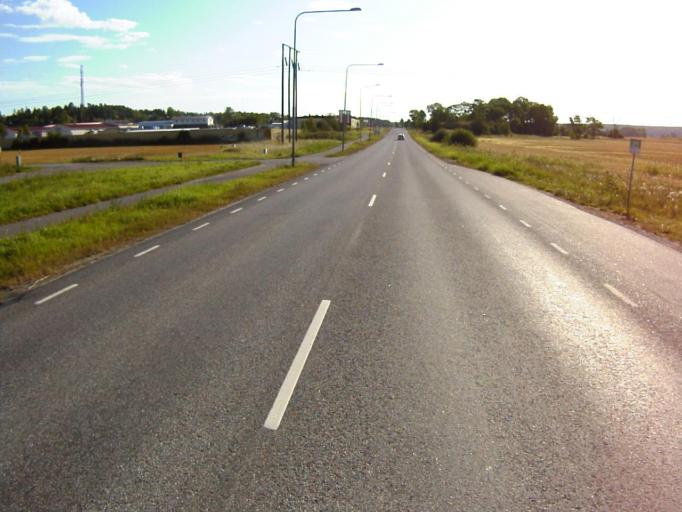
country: SE
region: Soedermanland
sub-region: Eskilstuna Kommun
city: Eskilstuna
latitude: 59.3758
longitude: 16.5673
